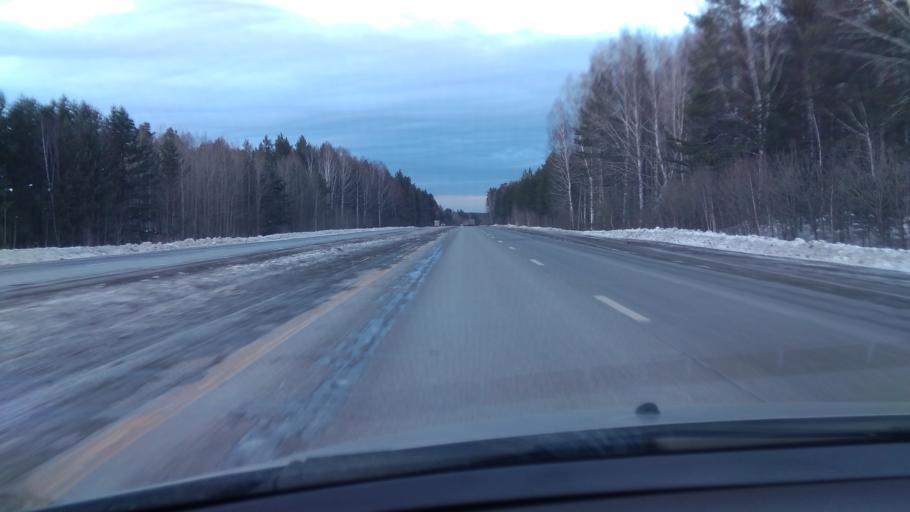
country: RU
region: Sverdlovsk
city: Shchelkun
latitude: 56.3292
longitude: 60.8692
